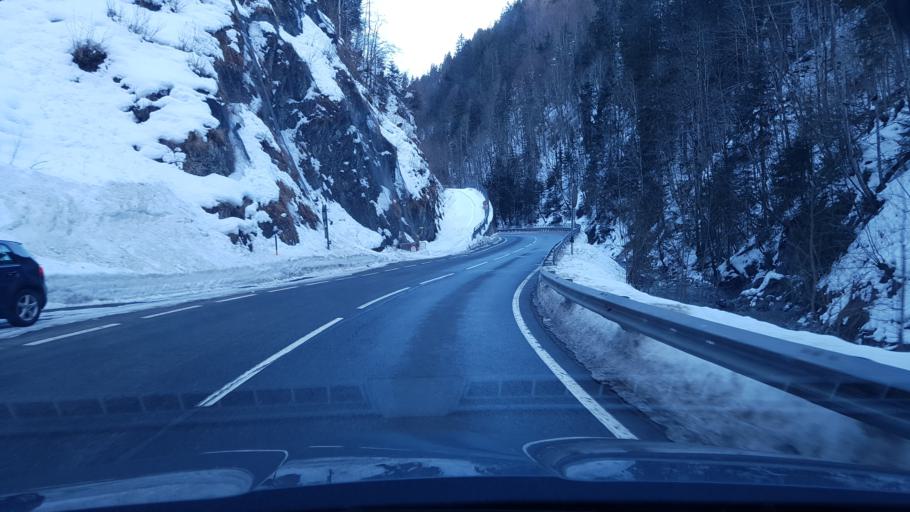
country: AT
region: Salzburg
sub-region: Politischer Bezirk Zell am See
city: Lend
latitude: 47.3328
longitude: 13.0210
